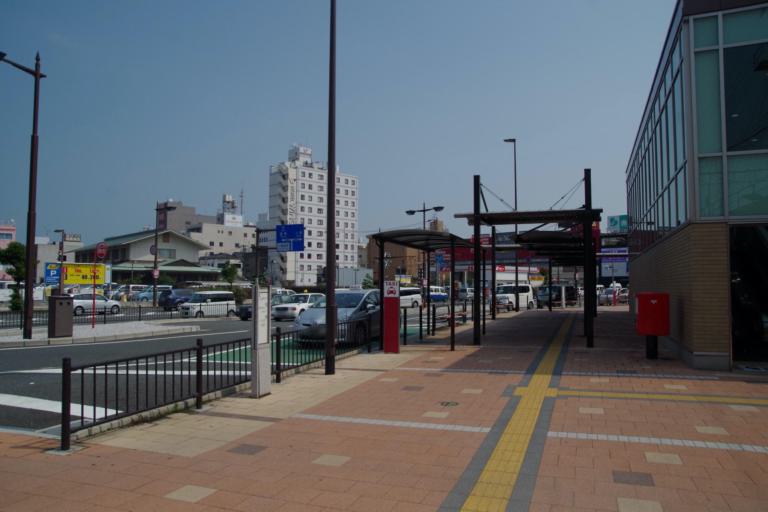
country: JP
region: Yamaguchi
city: Shimonoseki
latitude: 33.9505
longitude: 130.9219
